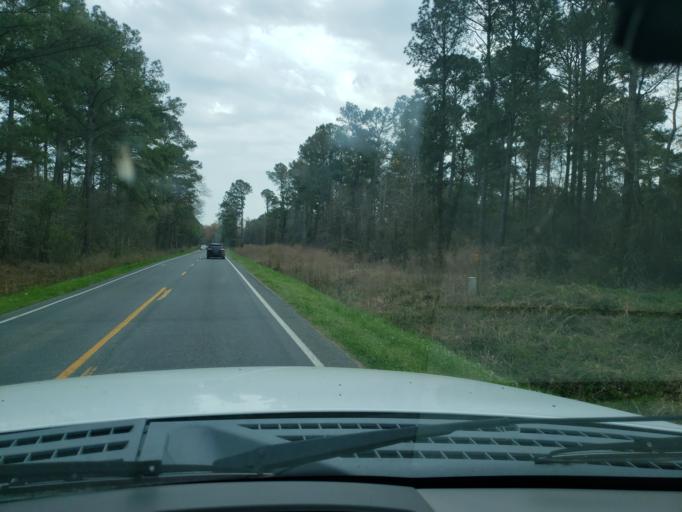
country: US
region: North Carolina
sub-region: Duplin County
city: Wallace
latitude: 34.7944
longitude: -77.8605
